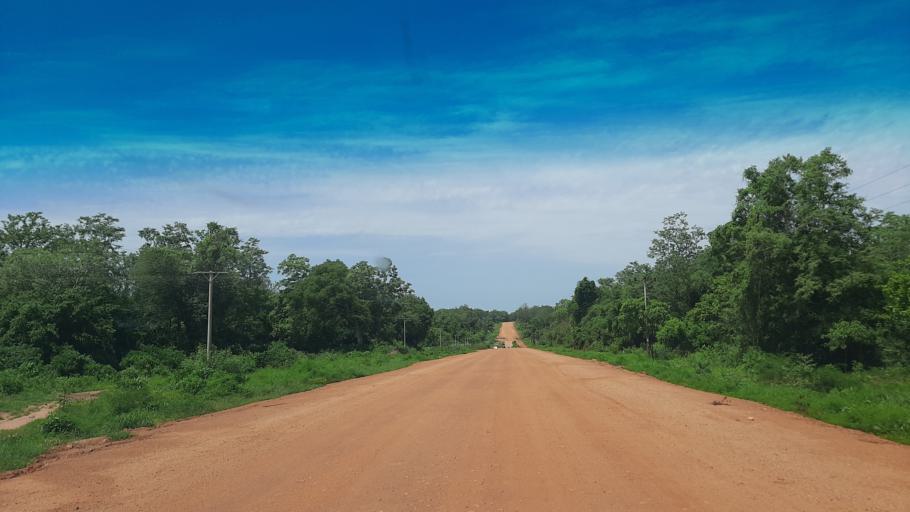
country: ET
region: Gambela
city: Gambela
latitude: 8.0923
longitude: 34.5889
